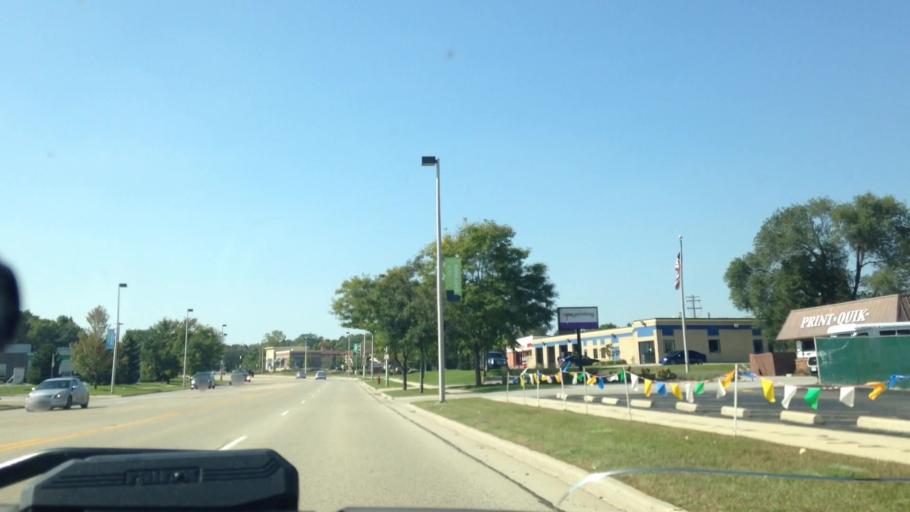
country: US
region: Wisconsin
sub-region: Waukesha County
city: Menomonee Falls
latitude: 43.1785
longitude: -88.0997
